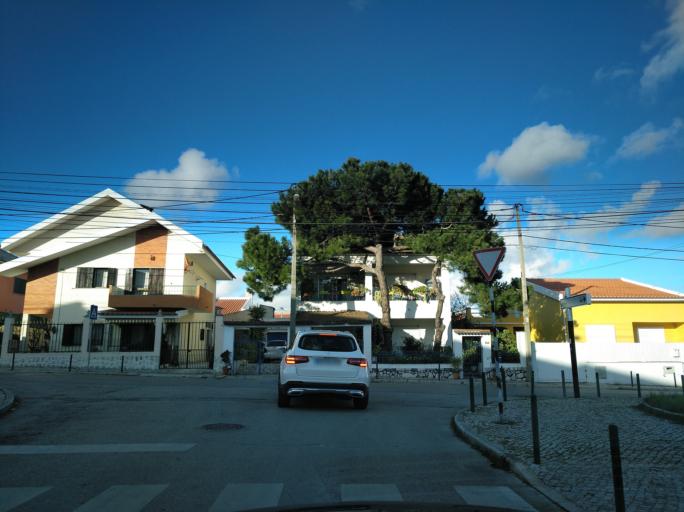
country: PT
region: Setubal
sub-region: Almada
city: Sobreda
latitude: 38.6446
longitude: -9.1862
